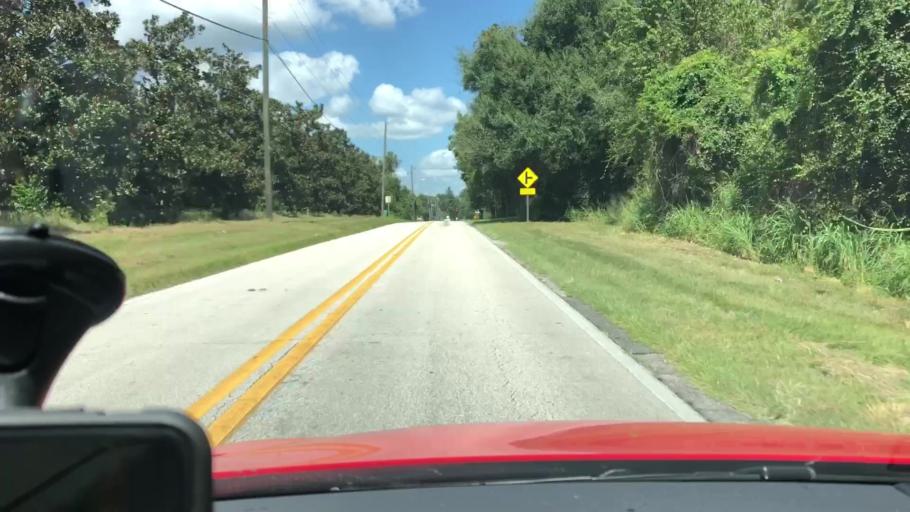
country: US
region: Florida
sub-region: Volusia County
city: North DeLand
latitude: 29.0522
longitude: -81.3166
